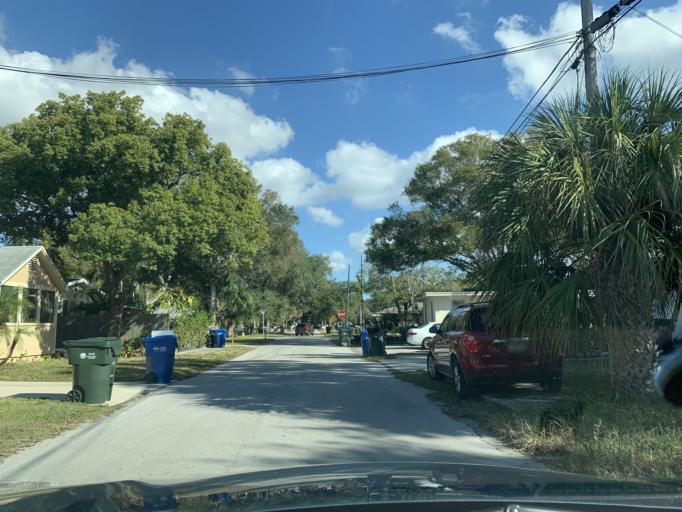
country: US
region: Florida
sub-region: Pinellas County
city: Belleair
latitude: 27.9285
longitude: -82.7944
